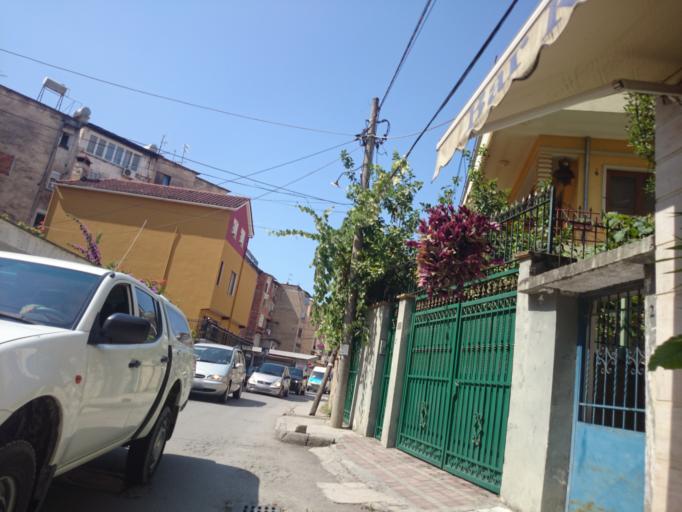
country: AL
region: Tirane
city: Tirana
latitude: 41.3265
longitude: 19.8314
